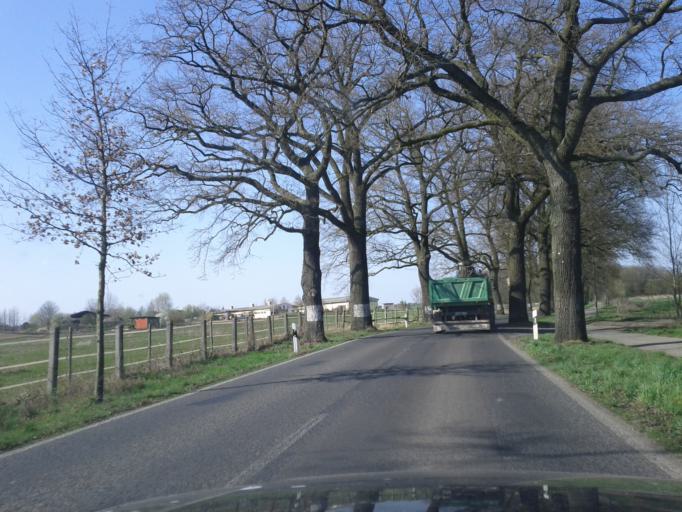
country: DE
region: Brandenburg
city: Schoneiche
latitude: 52.4823
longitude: 13.6938
